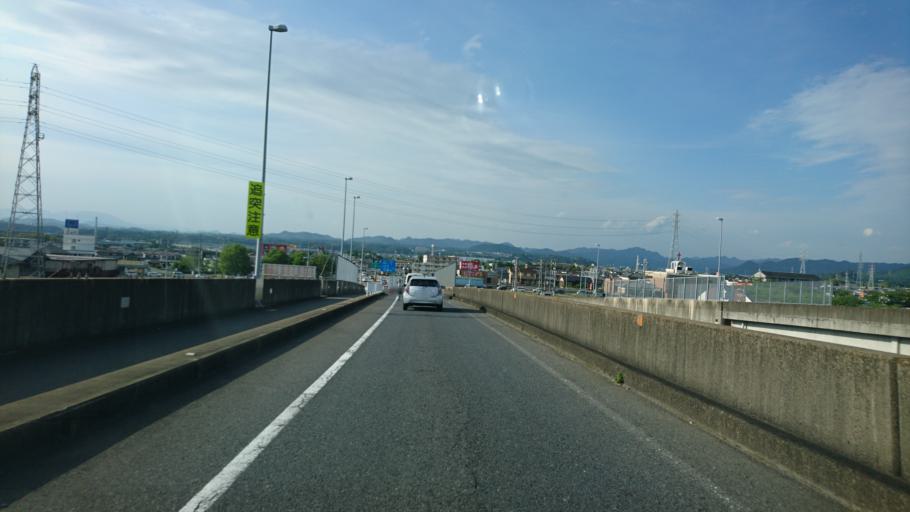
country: JP
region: Gifu
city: Minokamo
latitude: 35.4318
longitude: 137.0425
